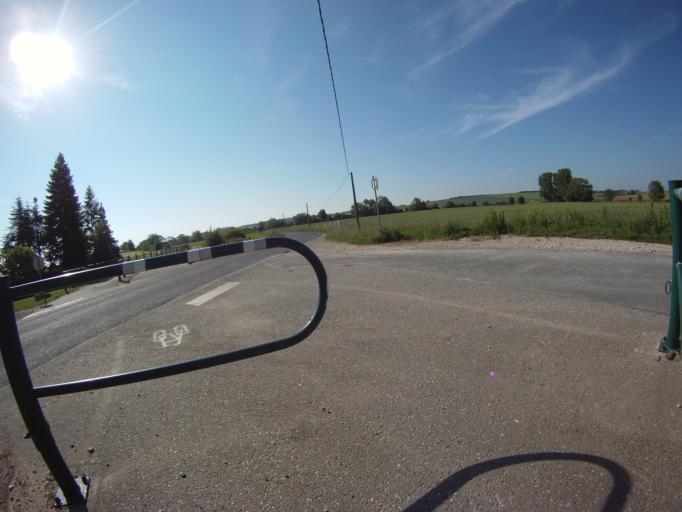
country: FR
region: Lorraine
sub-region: Departement de Meurthe-et-Moselle
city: Seichamps
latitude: 48.7414
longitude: 6.2871
